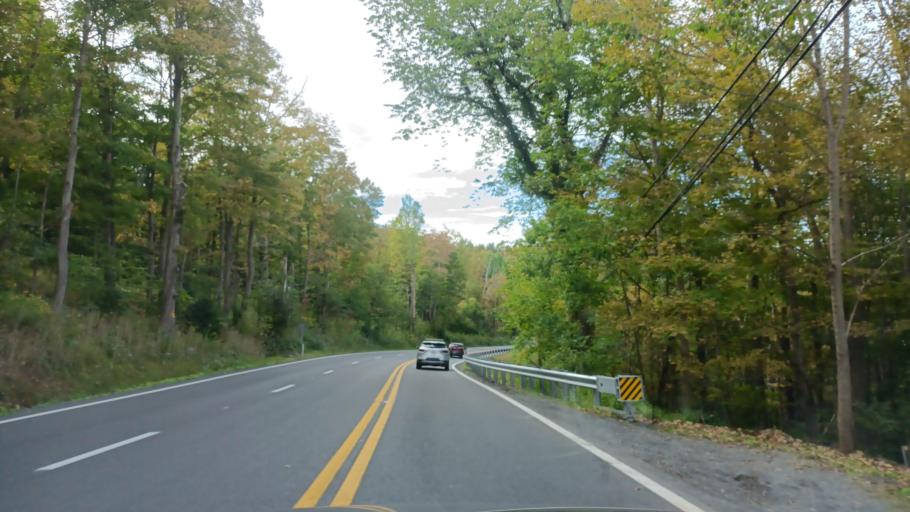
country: US
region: Maryland
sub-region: Garrett County
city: Mountain Lake Park
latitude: 39.2944
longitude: -79.3368
